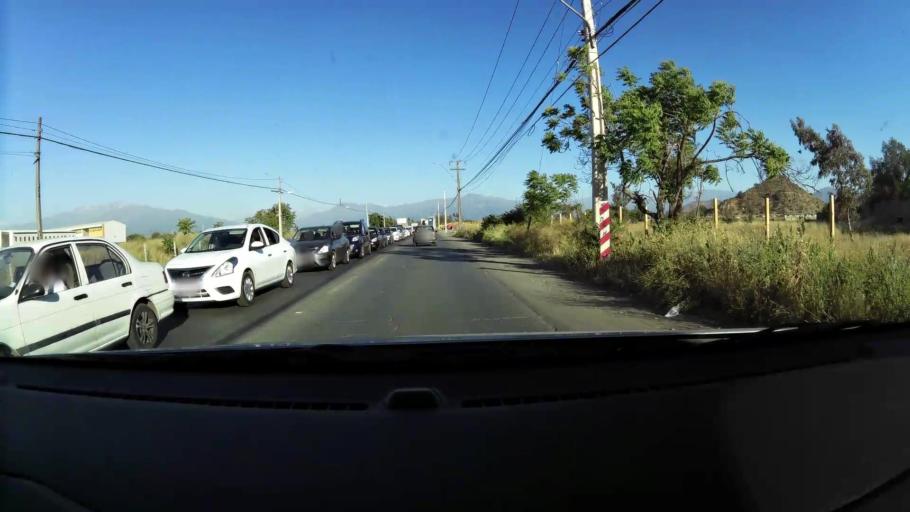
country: CL
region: Santiago Metropolitan
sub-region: Provincia de Maipo
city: San Bernardo
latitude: -33.6051
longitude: -70.6819
